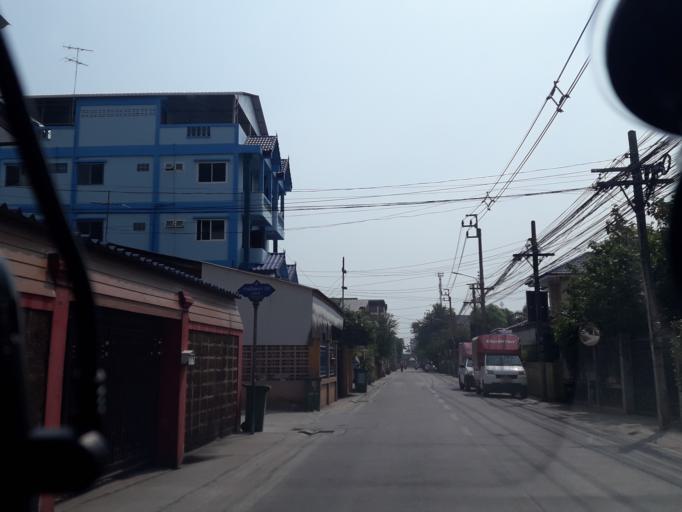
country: TH
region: Bangkok
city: Min Buri
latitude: 13.8160
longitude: 100.7051
